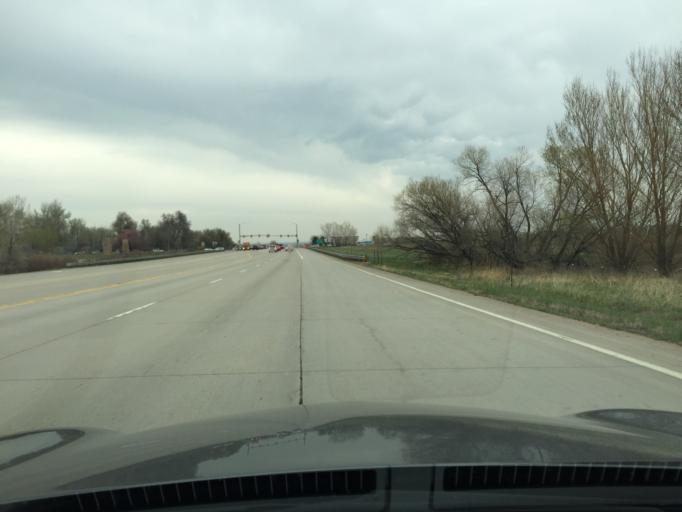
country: US
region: Colorado
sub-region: Boulder County
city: Lafayette
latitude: 40.0123
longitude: -105.1028
